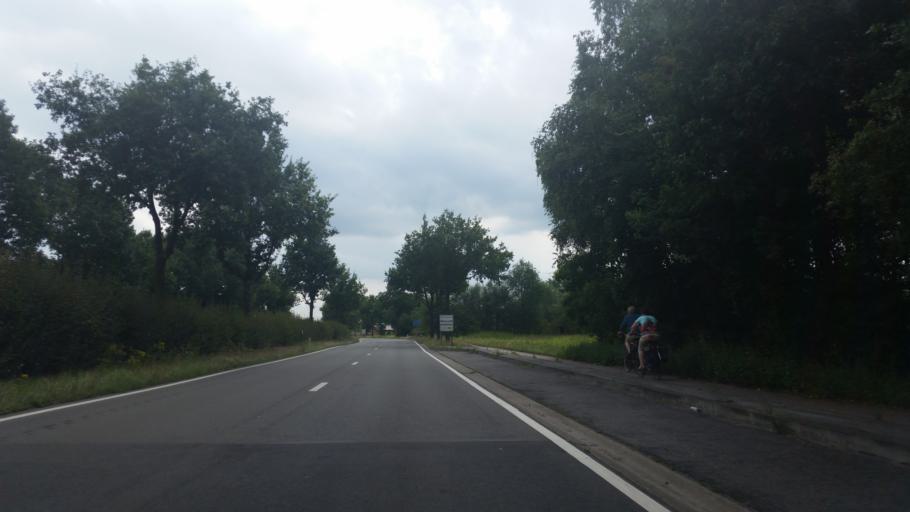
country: BE
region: Flanders
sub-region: Provincie Antwerpen
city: Kasterlee
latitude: 51.2729
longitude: 4.9552
